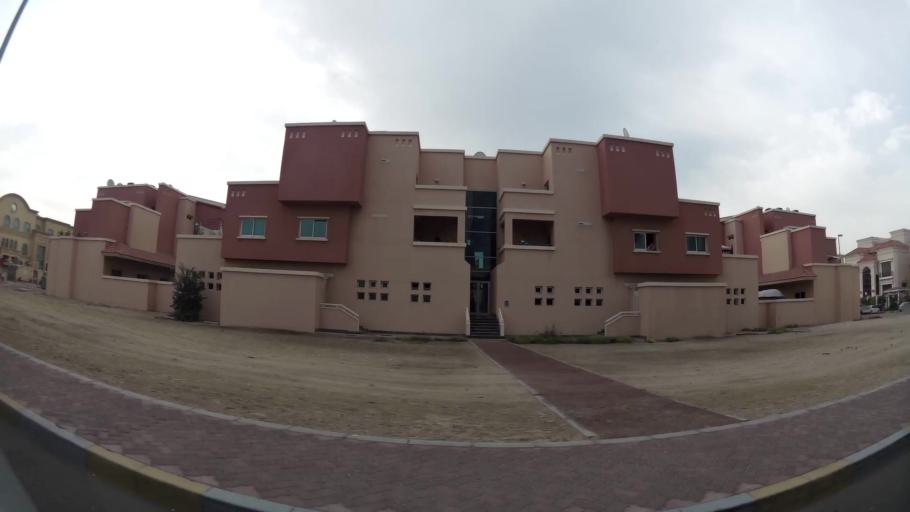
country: AE
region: Abu Dhabi
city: Abu Dhabi
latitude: 24.4745
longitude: 54.3794
